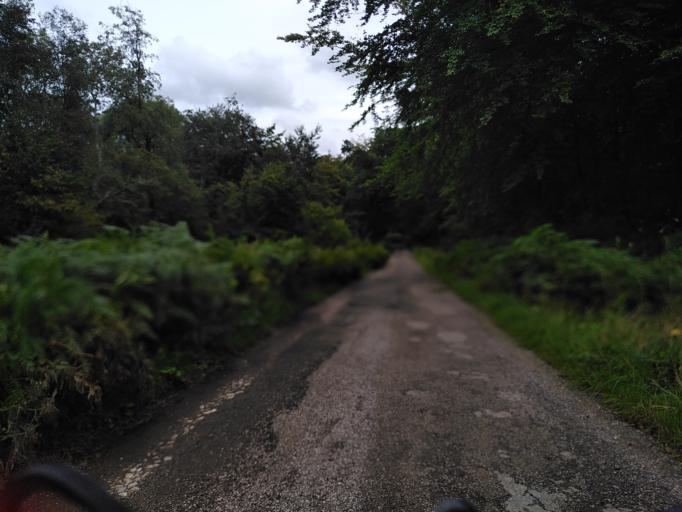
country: FR
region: Nord-Pas-de-Calais
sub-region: Departement du Pas-de-Calais
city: Desvres
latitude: 50.6869
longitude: 1.8244
